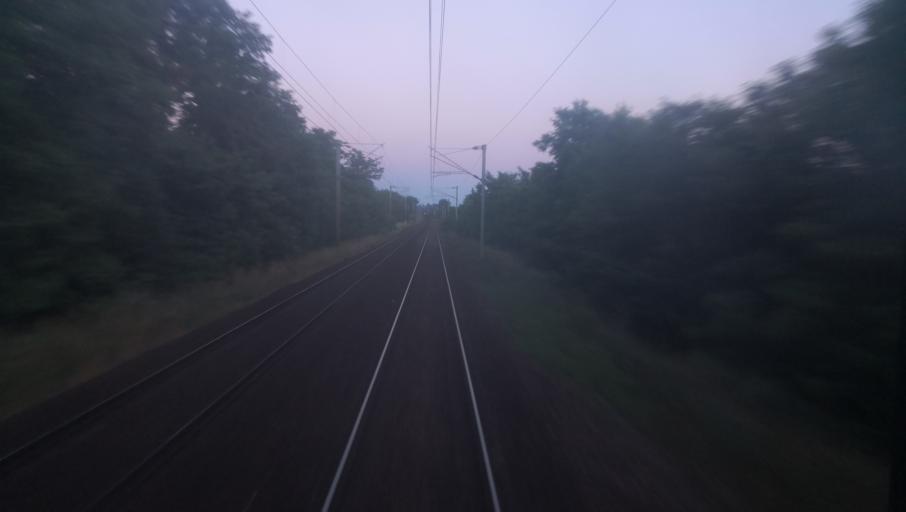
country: FR
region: Centre
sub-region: Departement du Loiret
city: Briare
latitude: 47.6530
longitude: 2.7248
